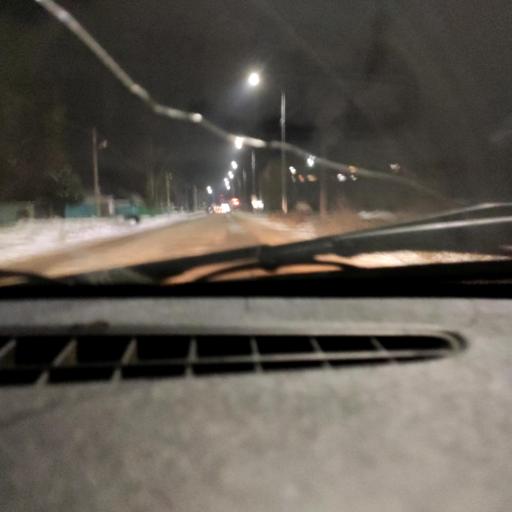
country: RU
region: Bashkortostan
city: Avdon
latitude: 54.6117
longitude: 55.8424
